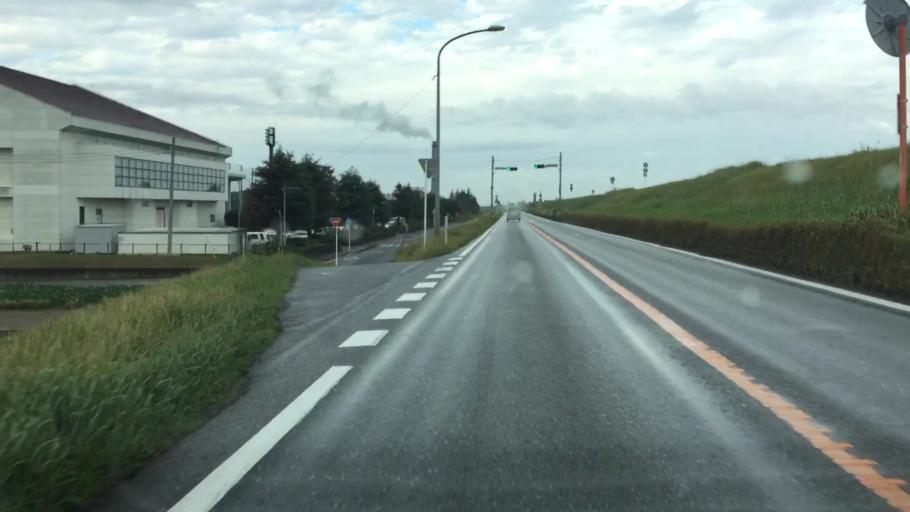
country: JP
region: Ibaraki
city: Toride
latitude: 35.8765
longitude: 140.1022
